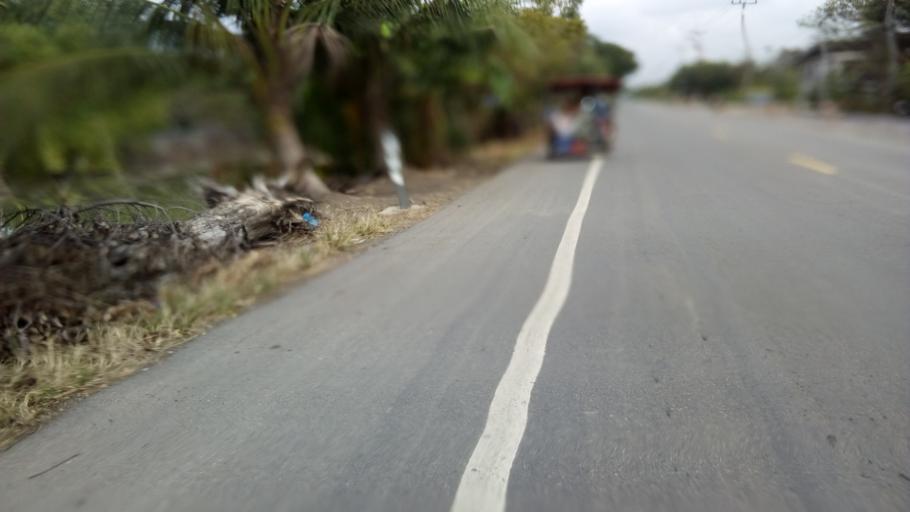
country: TH
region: Pathum Thani
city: Nong Suea
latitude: 14.1856
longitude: 100.8235
